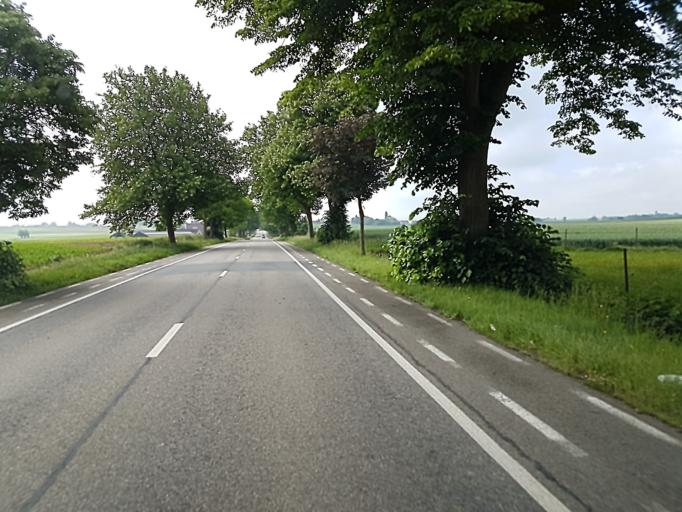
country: BE
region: Wallonia
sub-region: Province du Hainaut
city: Enghien
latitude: 50.6593
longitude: 4.0399
